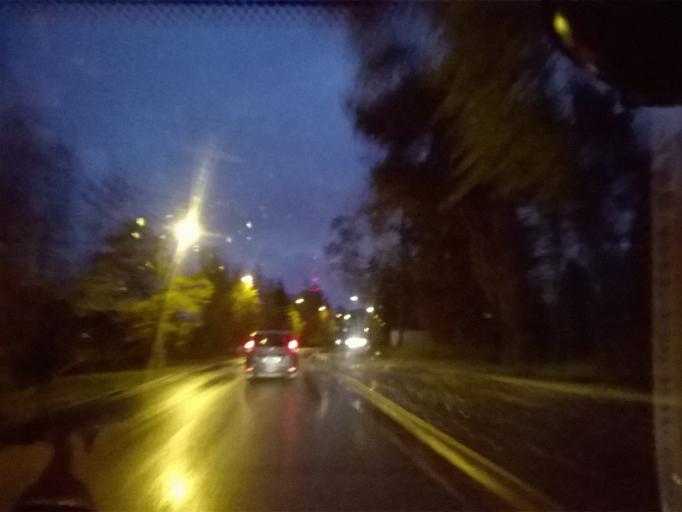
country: EE
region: Harju
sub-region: Viimsi vald
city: Viimsi
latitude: 59.4897
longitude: 24.8806
